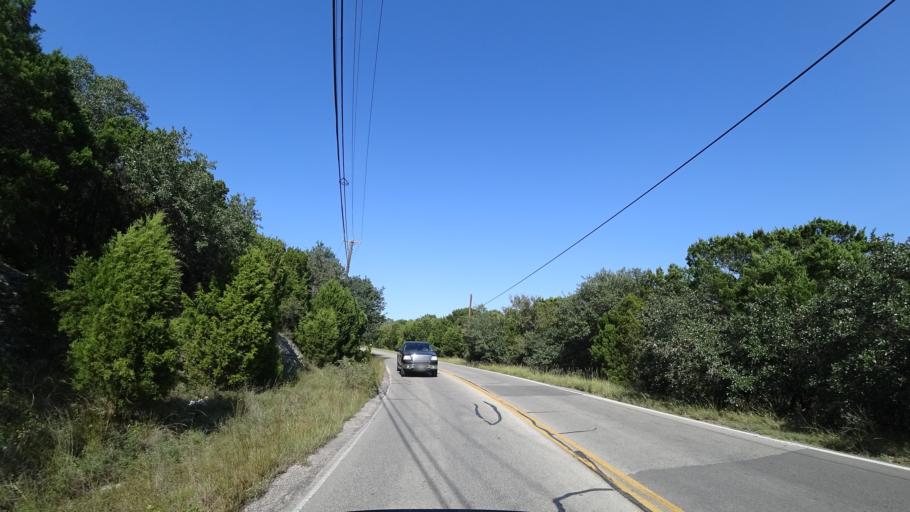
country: US
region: Texas
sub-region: Travis County
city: West Lake Hills
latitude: 30.2891
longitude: -97.8025
